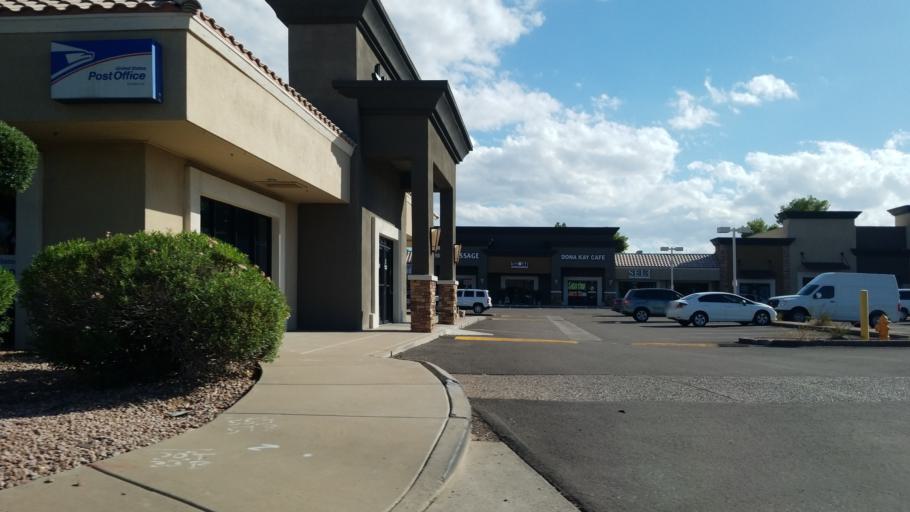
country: US
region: Arizona
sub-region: Maricopa County
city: Scottsdale
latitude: 33.5692
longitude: -111.8863
